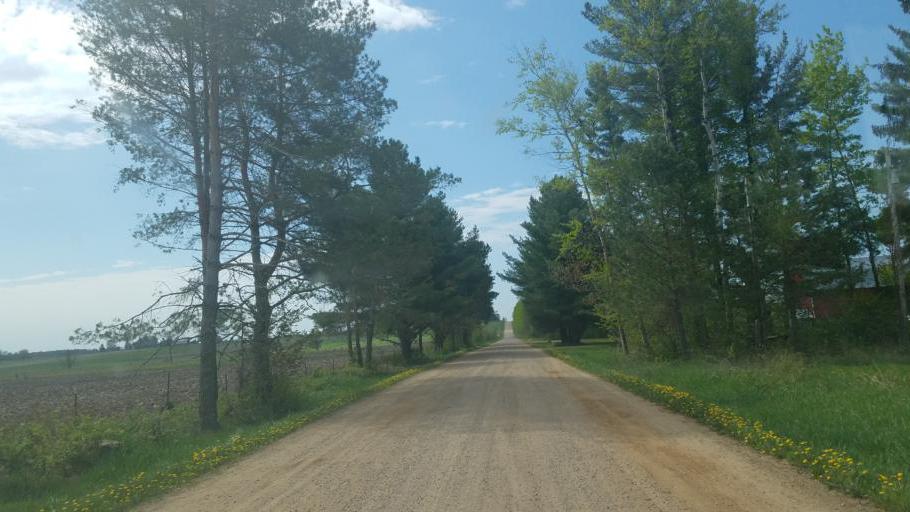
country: US
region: Wisconsin
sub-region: Marathon County
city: Spencer
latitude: 44.6077
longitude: -90.3766
